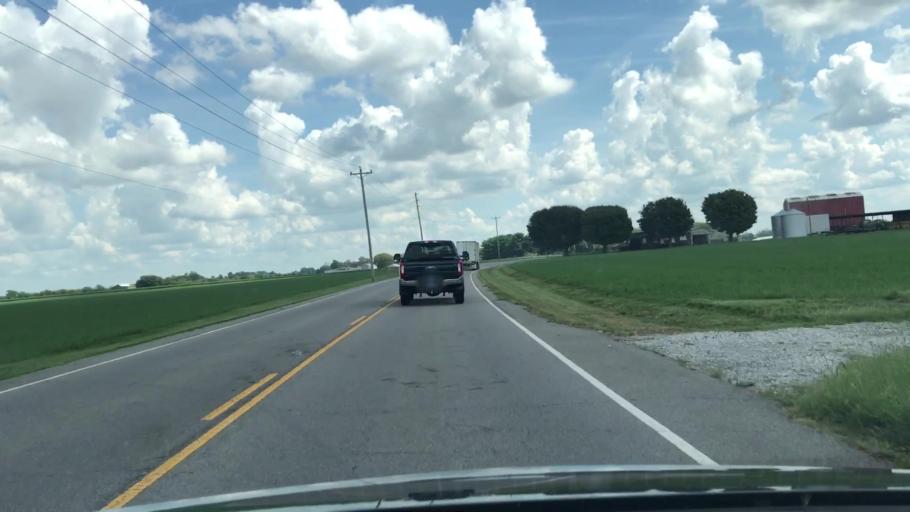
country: US
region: Tennessee
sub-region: Robertson County
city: Cross Plains
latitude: 36.5553
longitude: -86.7921
